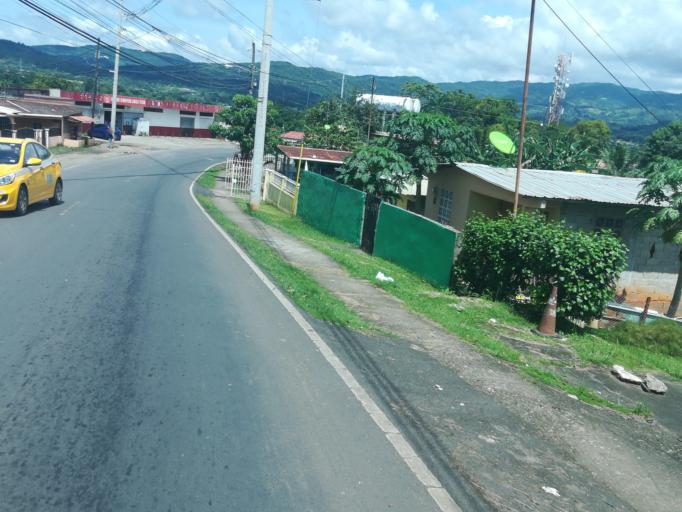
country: PA
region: Panama
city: Tocumen
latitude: 9.0908
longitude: -79.4070
